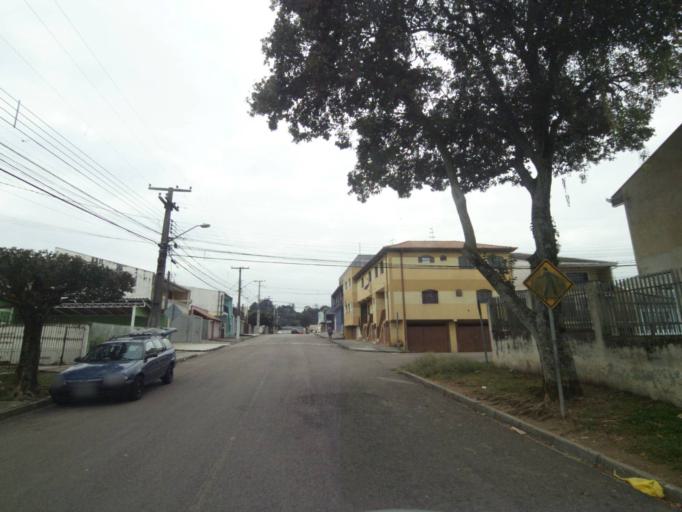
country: BR
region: Parana
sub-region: Curitiba
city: Curitiba
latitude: -25.5144
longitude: -49.3256
